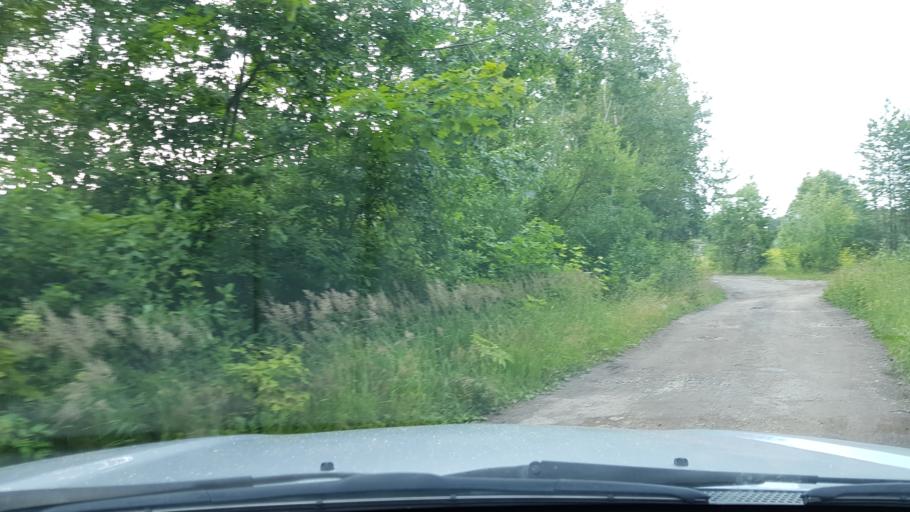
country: EE
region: Ida-Virumaa
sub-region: Narva-Joesuu linn
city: Narva-Joesuu
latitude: 59.4580
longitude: 28.0644
